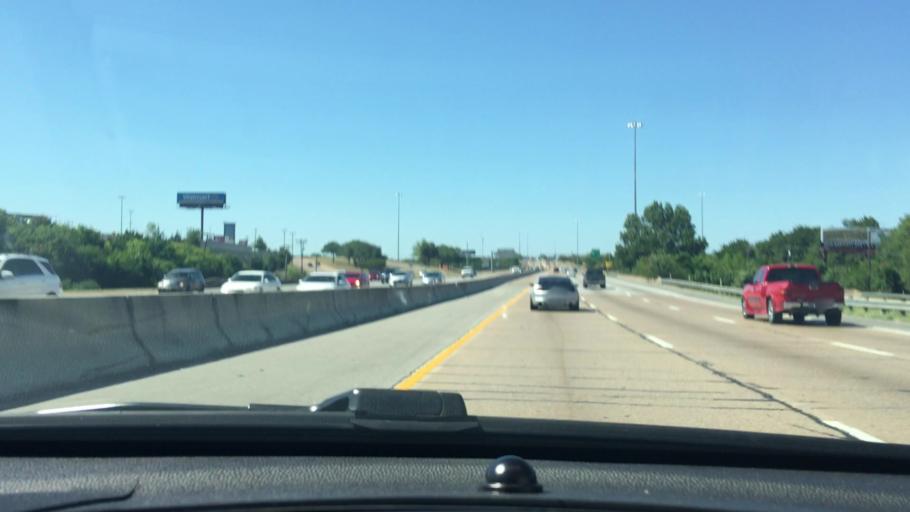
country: US
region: Texas
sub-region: Dallas County
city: Cockrell Hill
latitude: 32.6821
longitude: -96.8230
